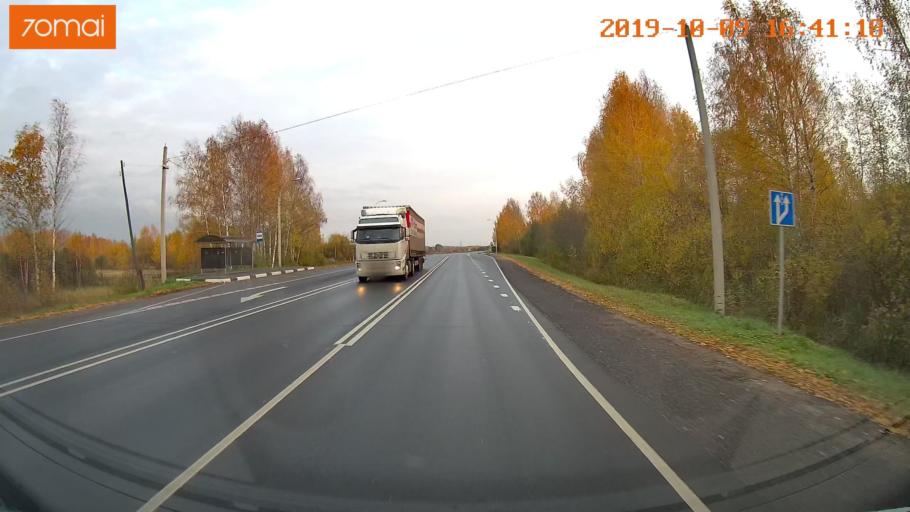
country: RU
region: Kostroma
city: Volgorechensk
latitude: 57.4743
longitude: 41.0783
